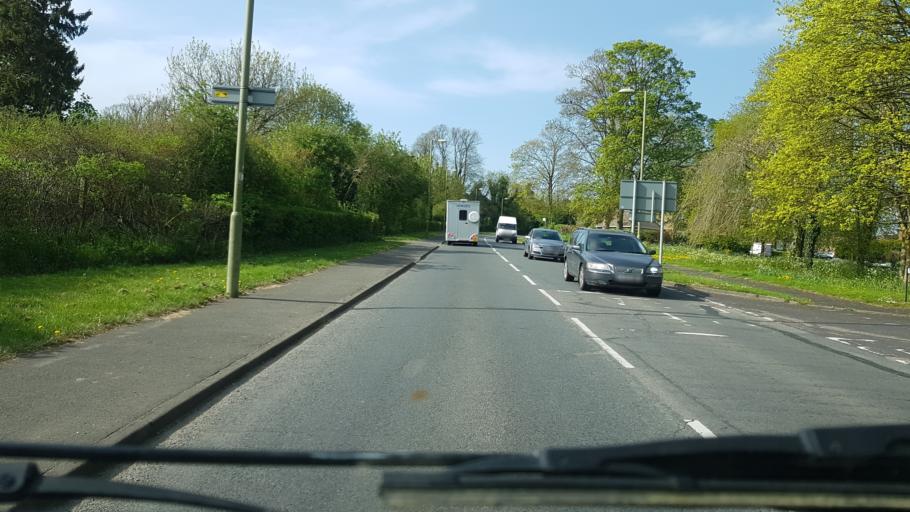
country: GB
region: England
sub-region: Hampshire
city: Basingstoke
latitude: 51.2624
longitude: -1.1375
